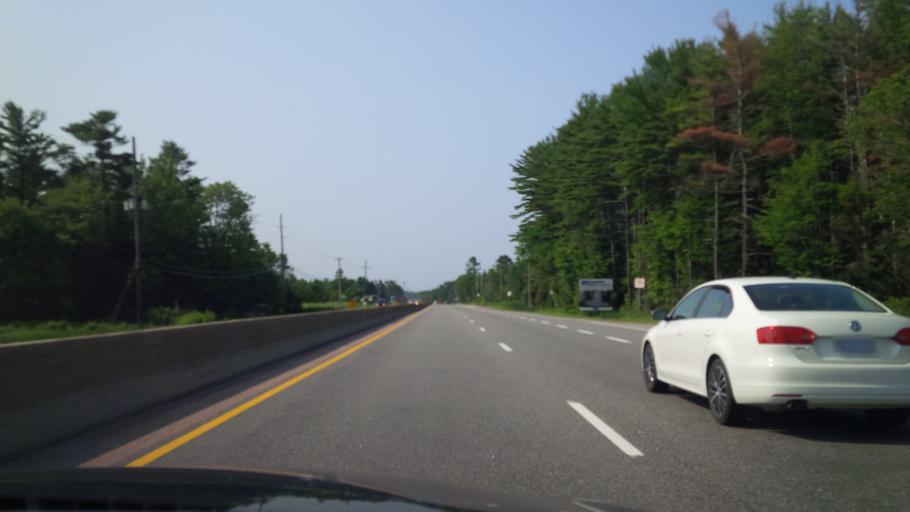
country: CA
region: Ontario
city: Gravenhurst
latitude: 44.8426
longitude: -79.3179
